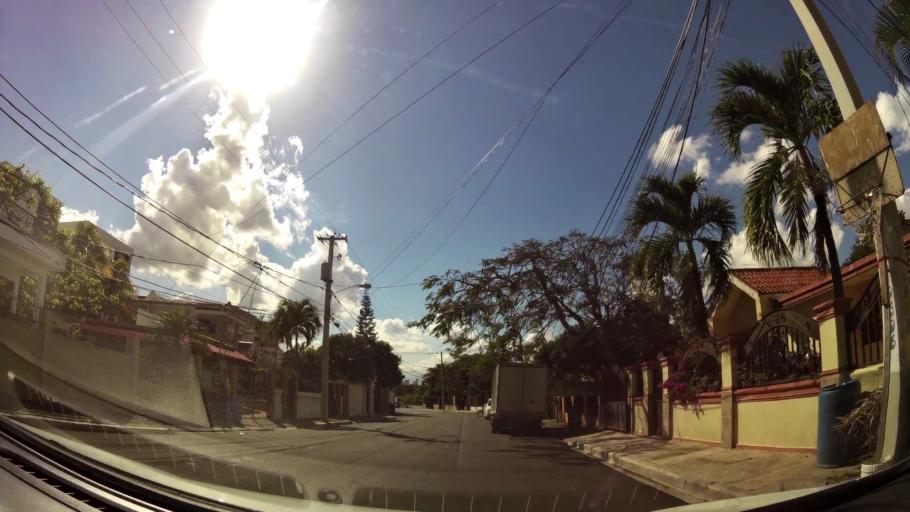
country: DO
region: Santiago
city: Santiago de los Caballeros
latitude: 19.4514
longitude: -70.6671
